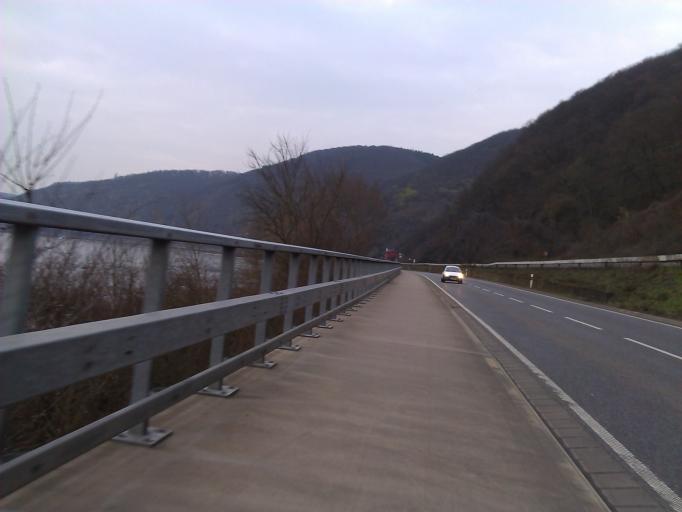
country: DE
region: Rheinland-Pfalz
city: Spay
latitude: 50.2469
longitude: 7.6474
